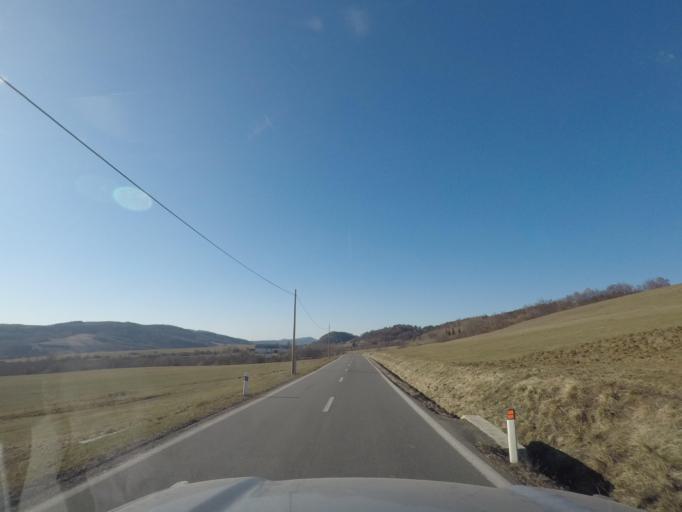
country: SK
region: Presovsky
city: Medzilaborce
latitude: 49.2173
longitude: 21.9822
